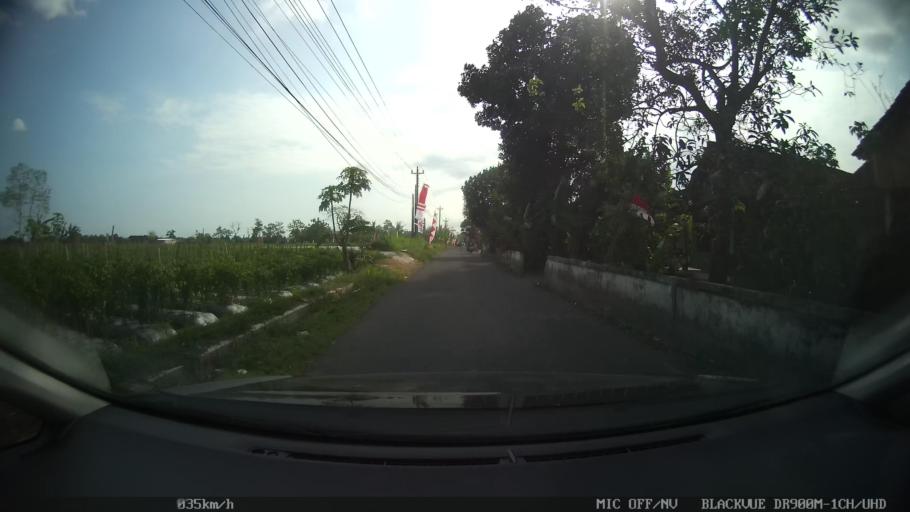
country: ID
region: Daerah Istimewa Yogyakarta
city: Depok
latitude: -7.7369
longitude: 110.4487
